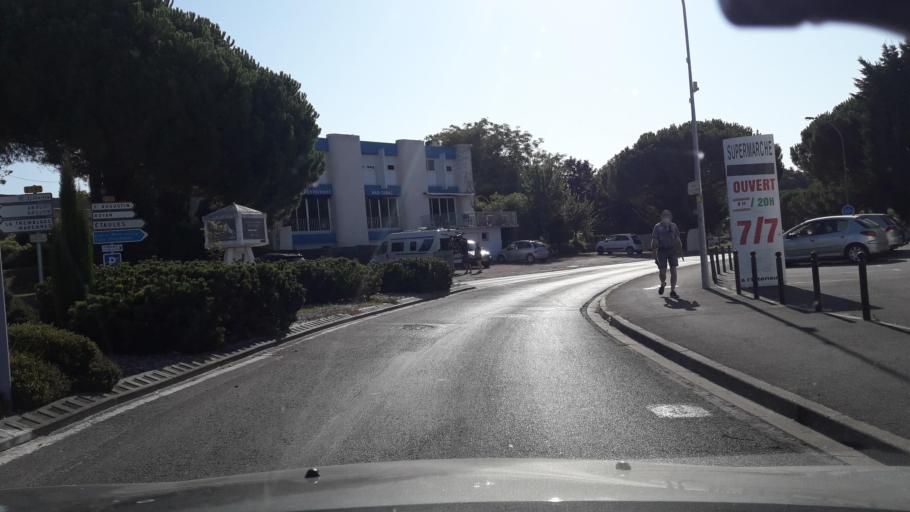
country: FR
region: Poitou-Charentes
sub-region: Departement de la Charente-Maritime
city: Les Mathes
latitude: 45.7164
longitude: -1.1511
